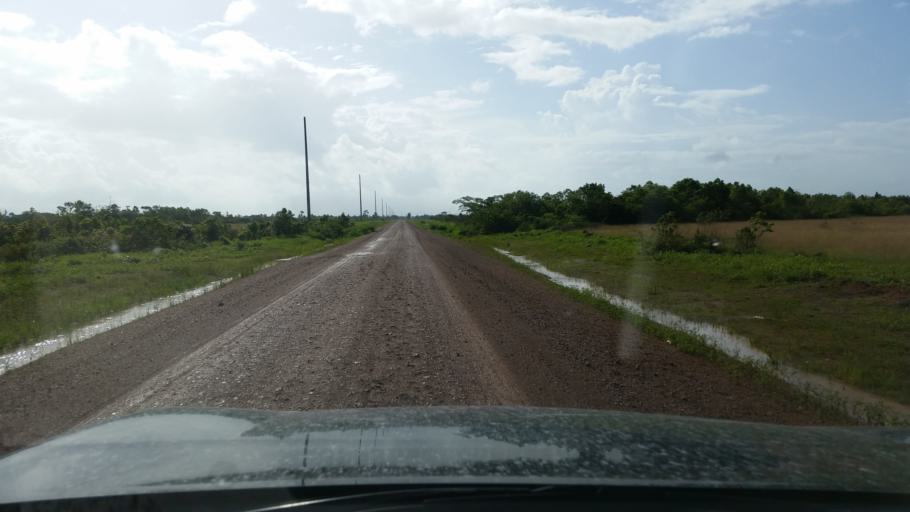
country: NI
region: Atlantico Norte (RAAN)
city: Puerto Cabezas
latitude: 14.1092
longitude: -83.5848
